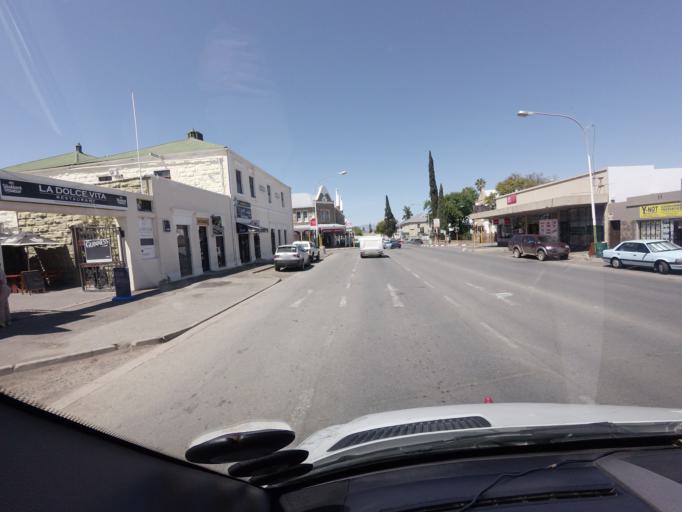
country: ZA
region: Western Cape
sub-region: Eden District Municipality
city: Oudtshoorn
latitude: -33.5880
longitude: 22.2035
